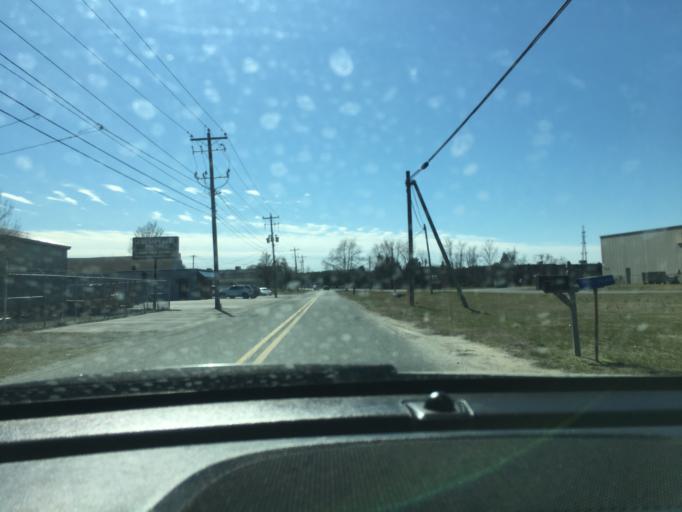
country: US
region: Maryland
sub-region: Wicomico County
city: Delmar
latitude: 38.4058
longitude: -75.5700
